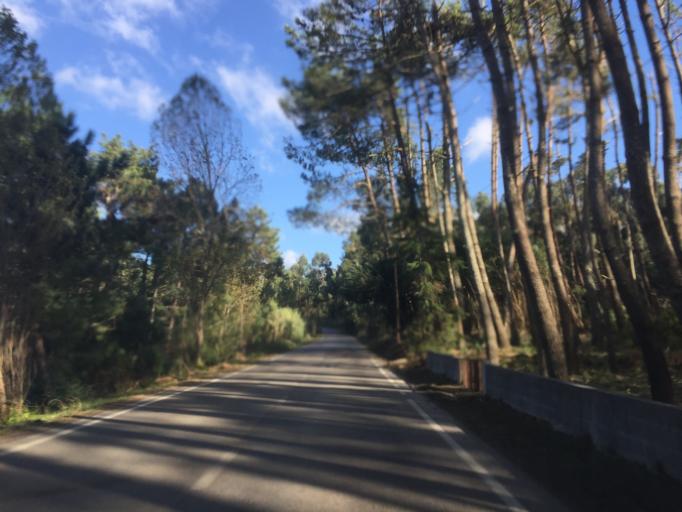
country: PT
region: Coimbra
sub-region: Figueira da Foz
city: Buarcos
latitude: 40.2159
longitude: -8.8767
